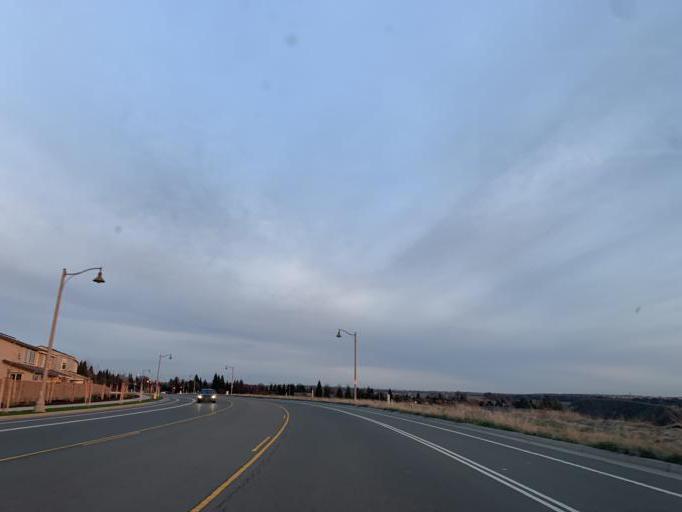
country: US
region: California
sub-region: Placer County
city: Lincoln
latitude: 38.8551
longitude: -121.2888
